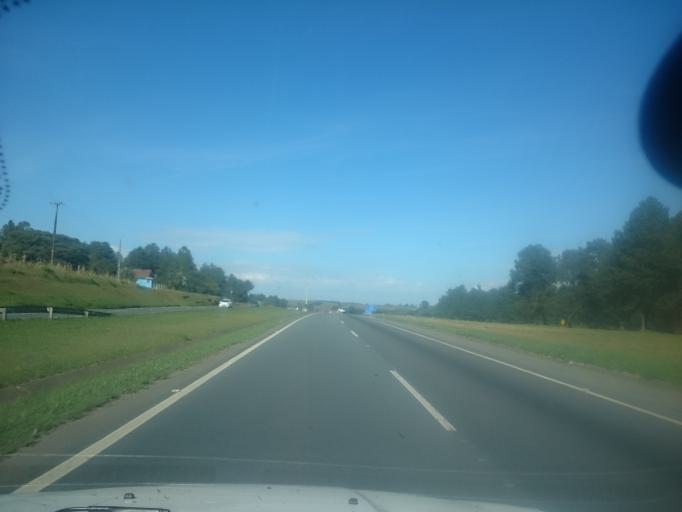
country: BR
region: Parana
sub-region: Campo Largo
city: Campo Largo
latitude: -25.4647
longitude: -49.7285
